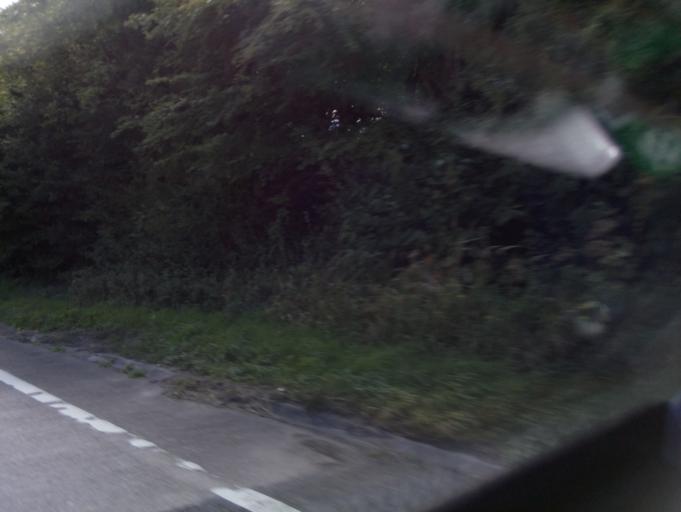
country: GB
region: England
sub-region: Dorset
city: Dorchester
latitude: 50.7493
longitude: -2.3570
